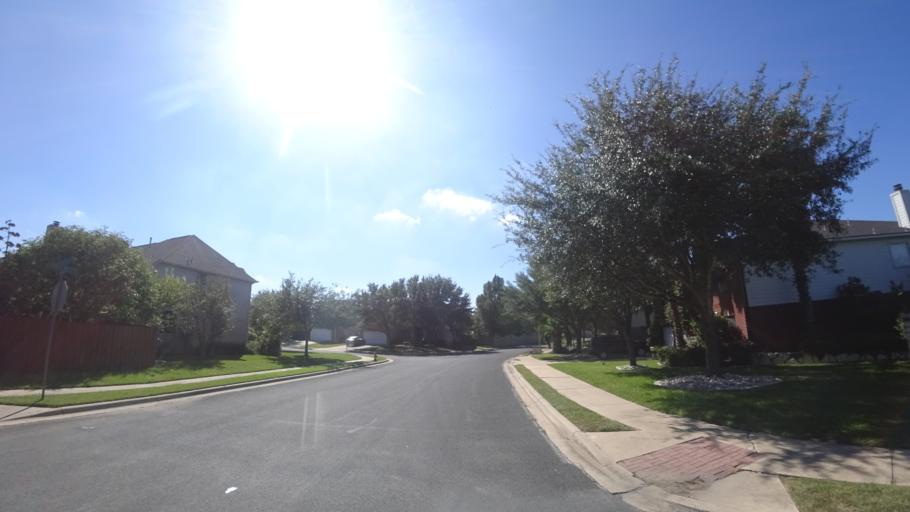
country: US
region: Texas
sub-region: Travis County
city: Manor
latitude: 30.3500
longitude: -97.6097
